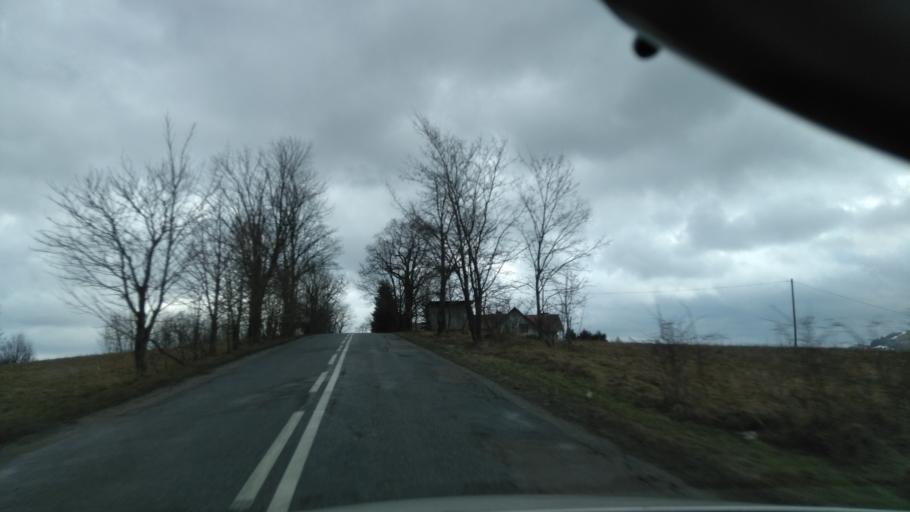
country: PL
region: Silesian Voivodeship
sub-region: Powiat cieszynski
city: Istebna
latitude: 49.5521
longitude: 18.9066
